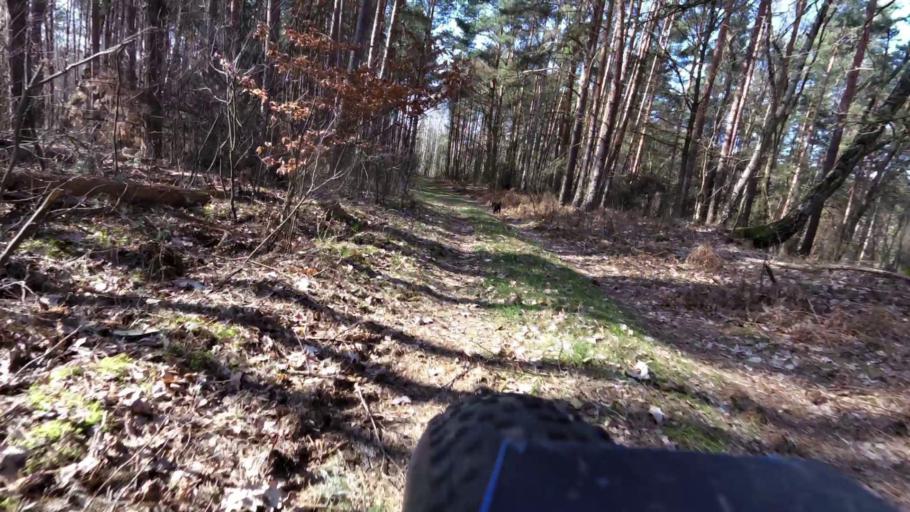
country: PL
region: Lubusz
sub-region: Powiat slubicki
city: Cybinka
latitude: 52.2280
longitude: 14.8299
